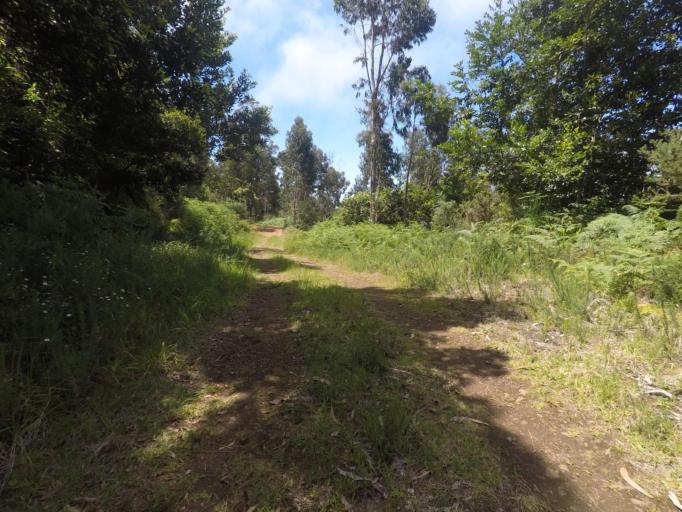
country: PT
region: Madeira
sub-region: Porto Moniz
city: Porto Moniz
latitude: 32.8395
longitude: -17.1464
